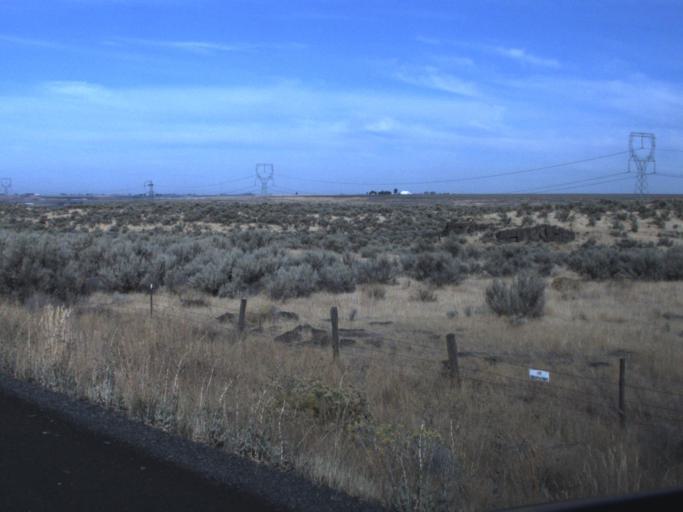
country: US
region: Washington
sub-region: Franklin County
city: Connell
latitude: 46.6315
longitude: -118.7503
